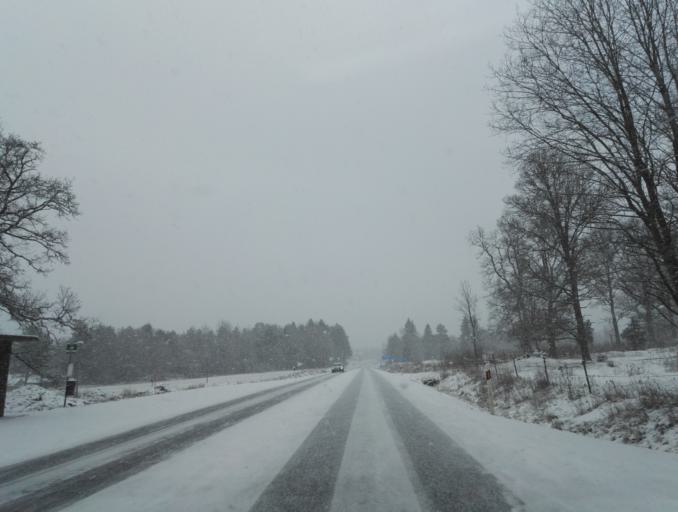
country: SE
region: Kronoberg
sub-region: Uppvidinge Kommun
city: Lenhovda
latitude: 57.0010
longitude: 15.2754
